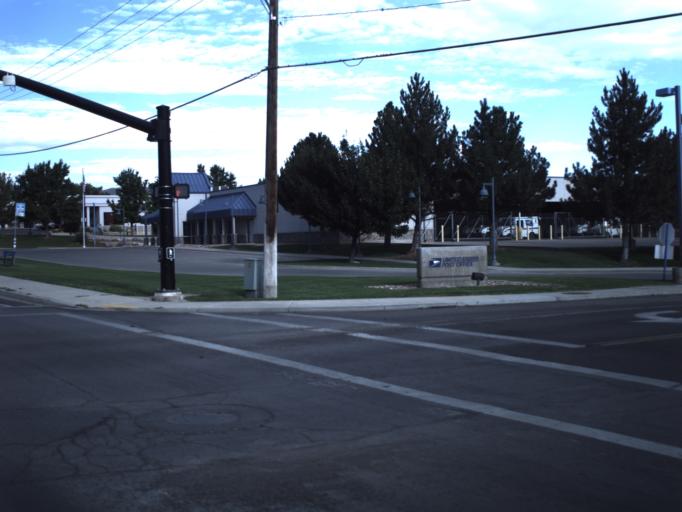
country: US
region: Utah
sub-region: Utah County
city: Payson
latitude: 40.0446
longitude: -111.7159
